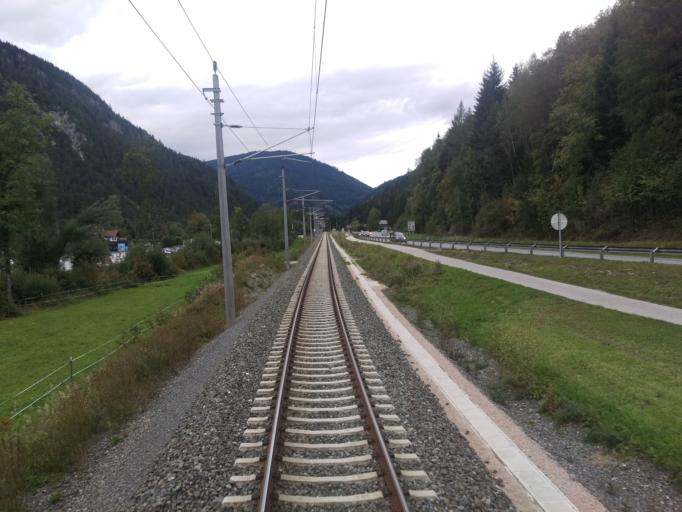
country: AT
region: Salzburg
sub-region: Politischer Bezirk Sankt Johann im Pongau
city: Forstau
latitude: 47.3888
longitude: 13.5993
